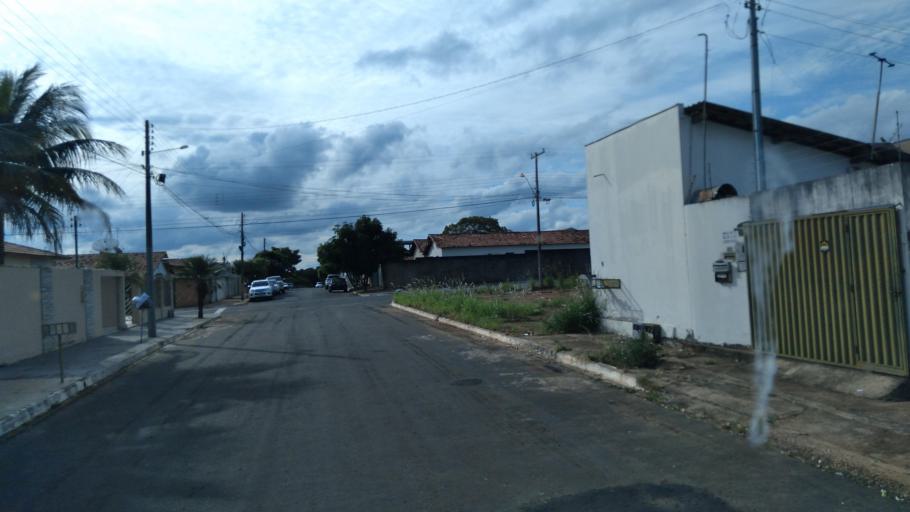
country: BR
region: Goias
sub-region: Mineiros
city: Mineiros
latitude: -17.5617
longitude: -52.5658
